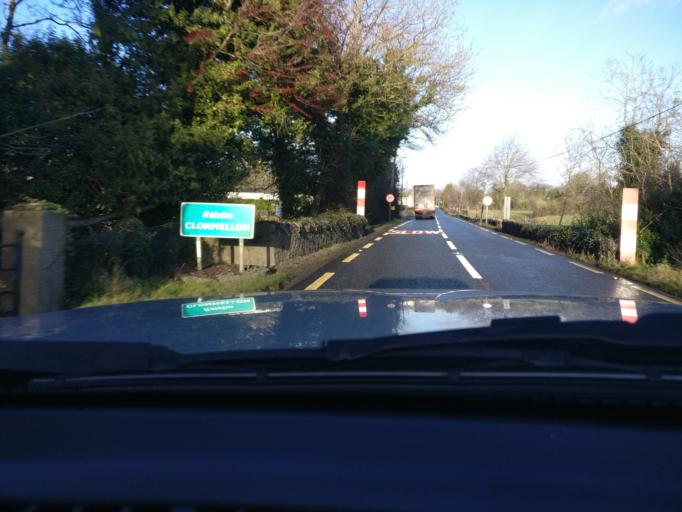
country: IE
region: Leinster
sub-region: An Mhi
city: Athboy
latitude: 53.6615
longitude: -7.0216
